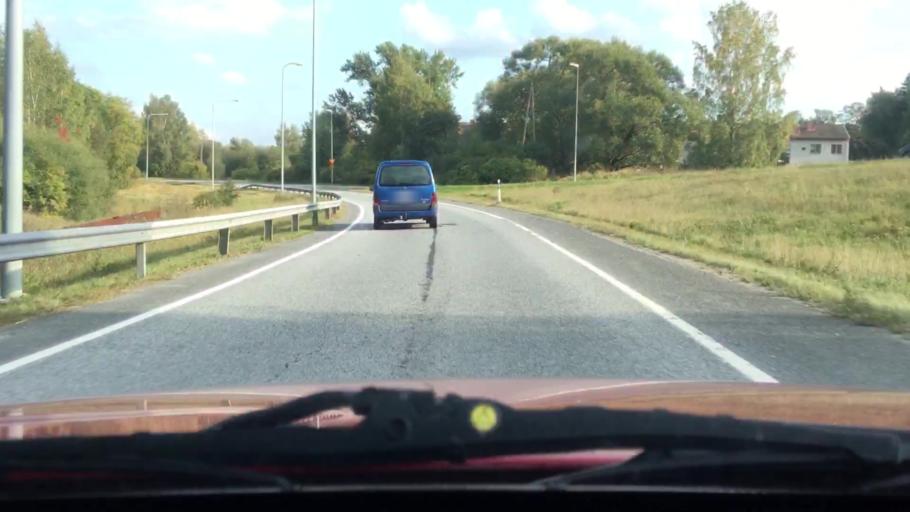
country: FI
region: Varsinais-Suomi
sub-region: Turku
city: Raisio
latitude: 60.4598
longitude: 22.2110
